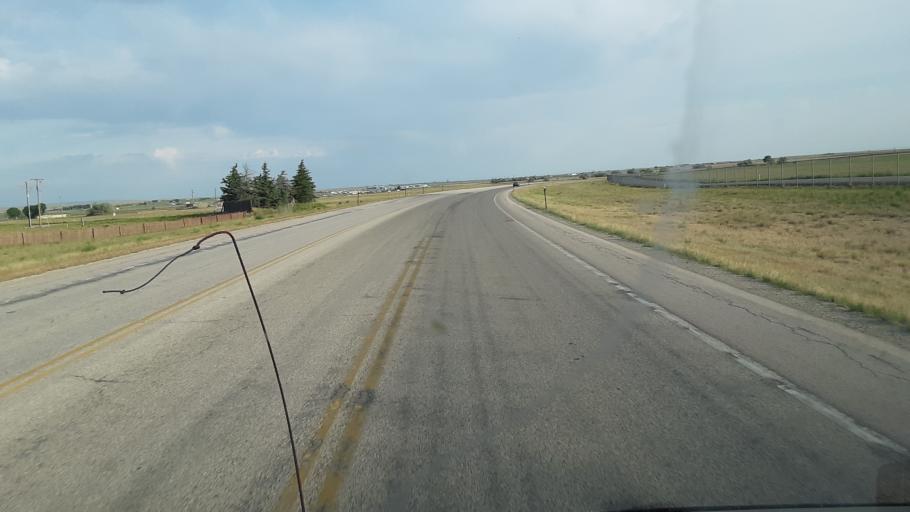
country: US
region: Wyoming
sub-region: Natrona County
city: Mills
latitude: 42.8919
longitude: -106.4794
